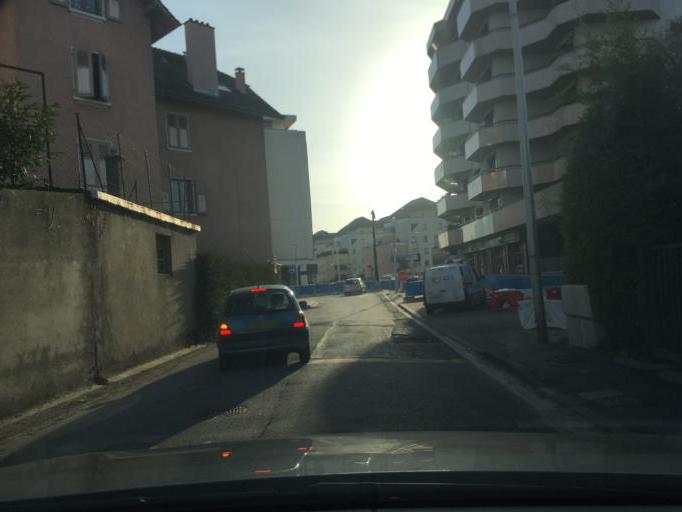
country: FR
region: Rhone-Alpes
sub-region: Departement de la Haute-Savoie
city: Gaillard
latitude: 46.1918
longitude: 6.2159
